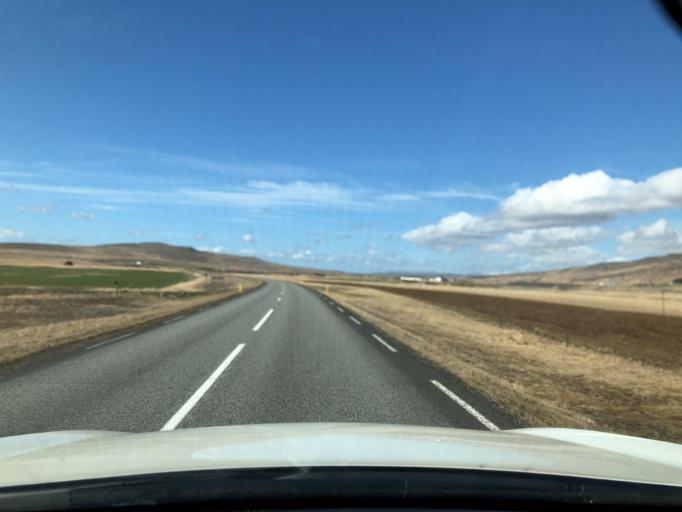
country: IS
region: South
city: Hveragerdi
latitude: 64.7016
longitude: -21.2101
